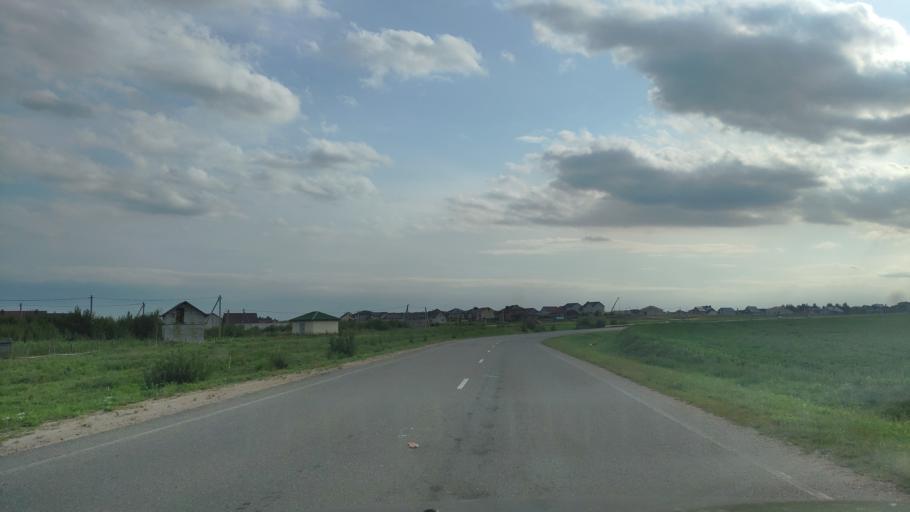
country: BY
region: Minsk
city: Azyartso
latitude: 53.8335
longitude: 27.3232
